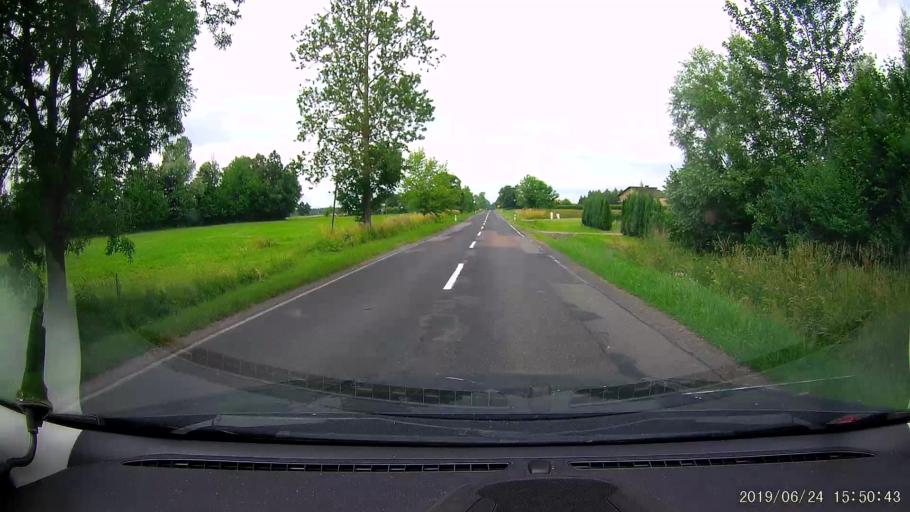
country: PL
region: Subcarpathian Voivodeship
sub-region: Powiat lubaczowski
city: Oleszyce
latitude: 50.1811
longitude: 23.0625
